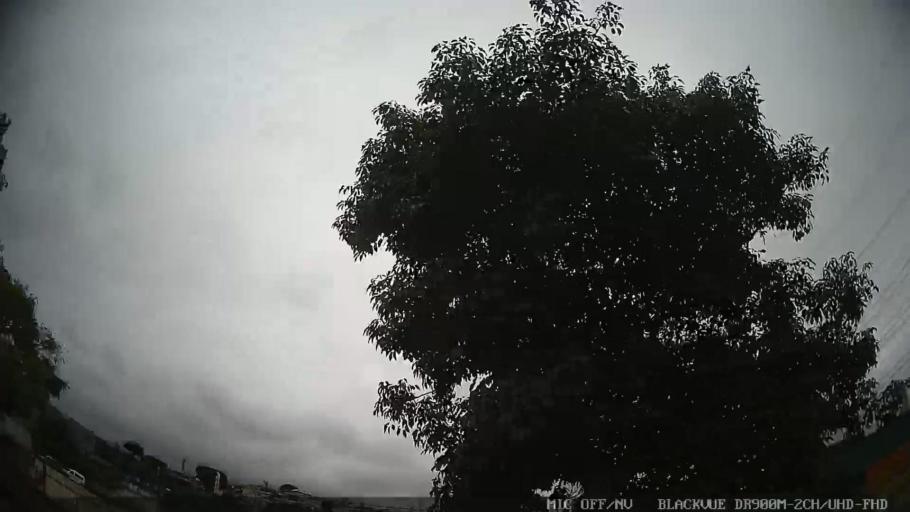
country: BR
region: Sao Paulo
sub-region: Osasco
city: Osasco
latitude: -23.4927
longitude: -46.7563
